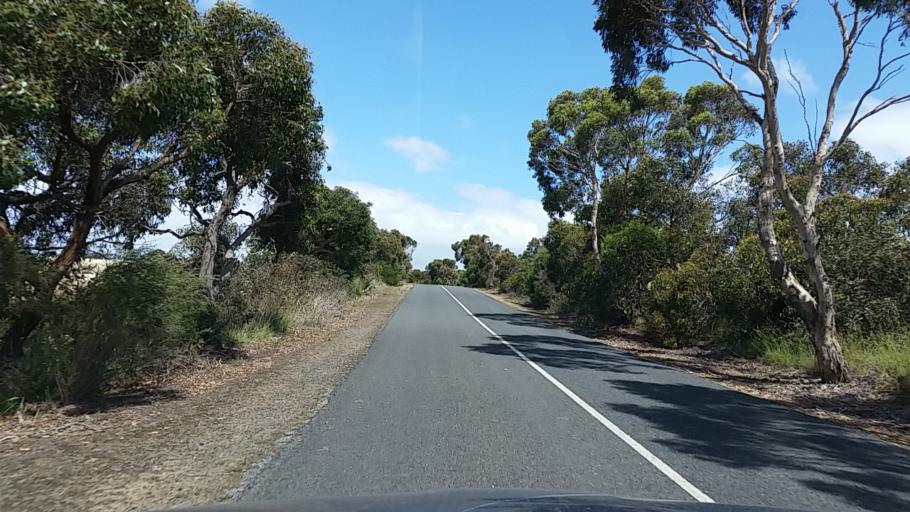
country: AU
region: South Australia
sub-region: Alexandrina
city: Port Elliot
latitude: -35.4496
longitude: 138.6303
